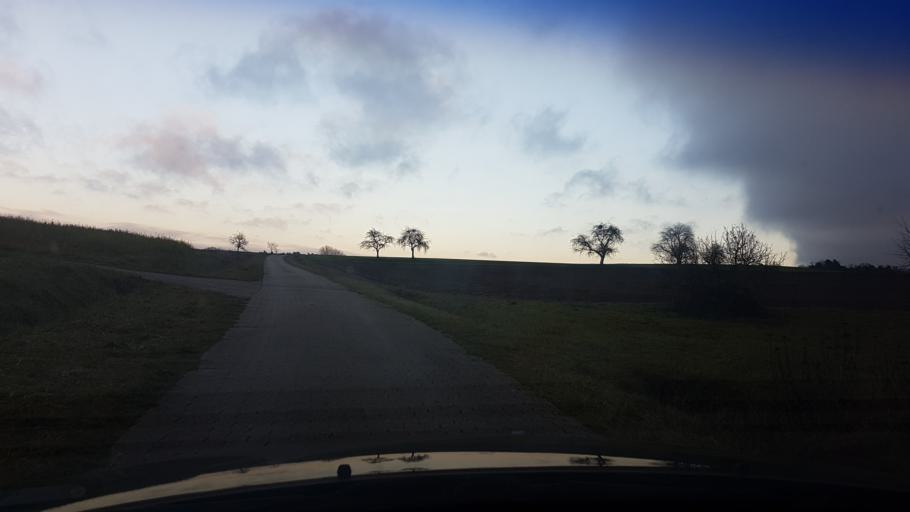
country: DE
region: Bavaria
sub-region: Upper Franconia
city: Lauter
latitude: 49.9473
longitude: 10.7677
